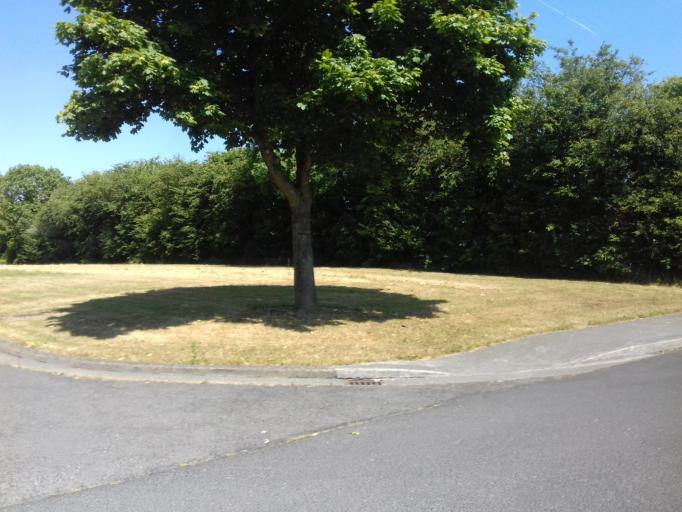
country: IE
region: Leinster
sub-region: An Mhi
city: Ashbourne
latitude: 53.5202
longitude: -6.3167
